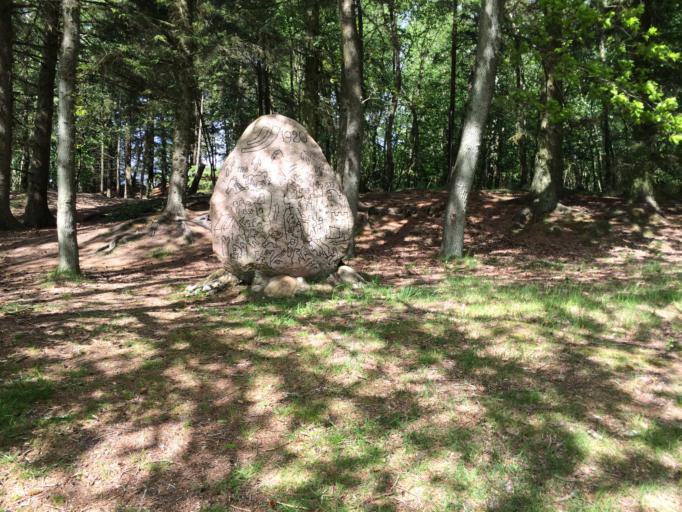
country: DK
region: Central Jutland
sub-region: Holstebro Kommune
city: Ulfborg
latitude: 56.2342
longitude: 8.4172
